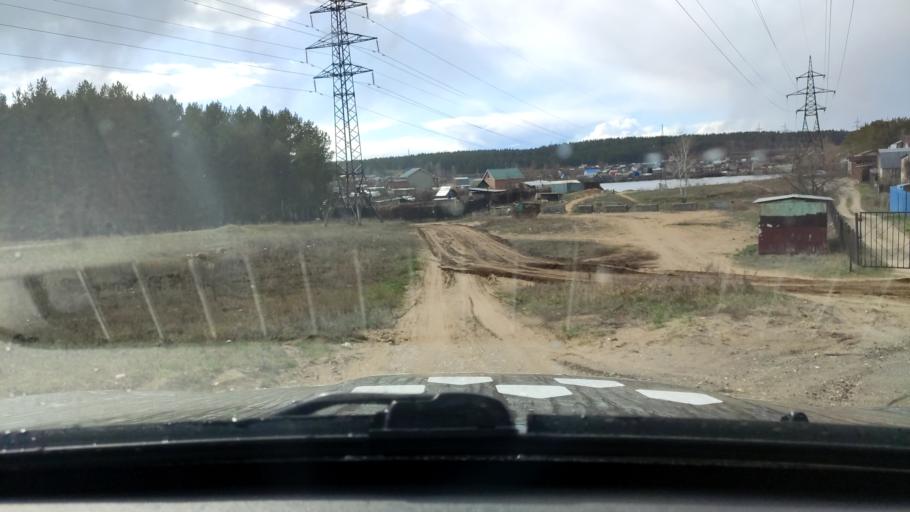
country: RU
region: Samara
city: Zhigulevsk
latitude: 53.4972
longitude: 49.5044
